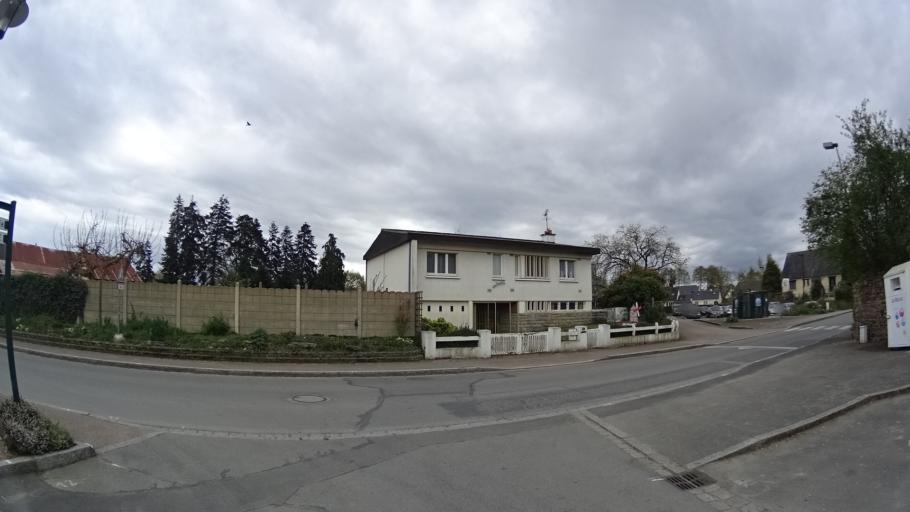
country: FR
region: Brittany
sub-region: Departement d'Ille-et-Vilaine
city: Cintre
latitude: 48.1053
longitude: -1.8721
